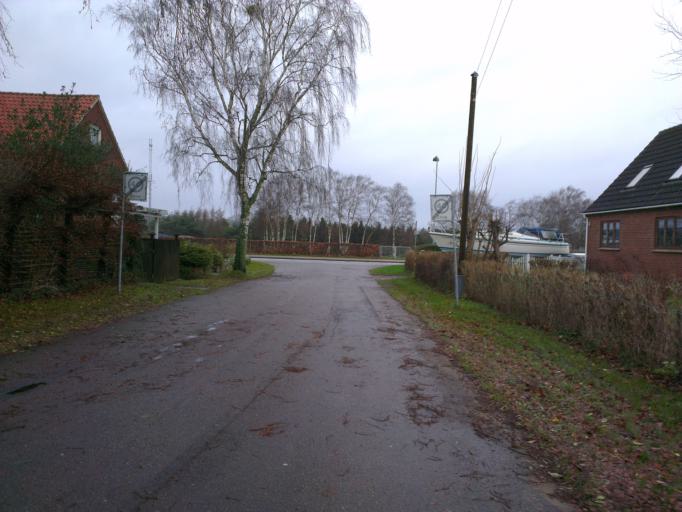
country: DK
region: Capital Region
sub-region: Frederikssund Kommune
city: Jaegerspris
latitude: 55.8547
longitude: 11.9925
